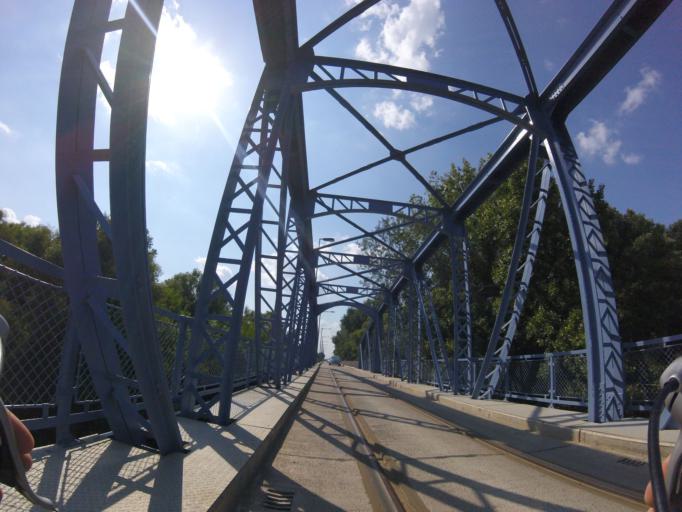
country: HU
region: Heves
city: Kiskore
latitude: 47.4790
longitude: 20.5133
